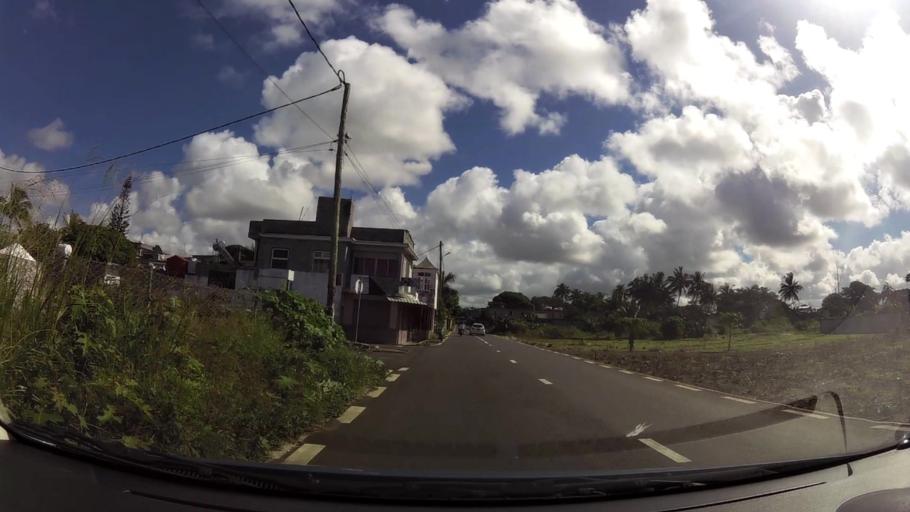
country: MU
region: Grand Port
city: Plaine Magnien
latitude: -20.4341
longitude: 57.6622
